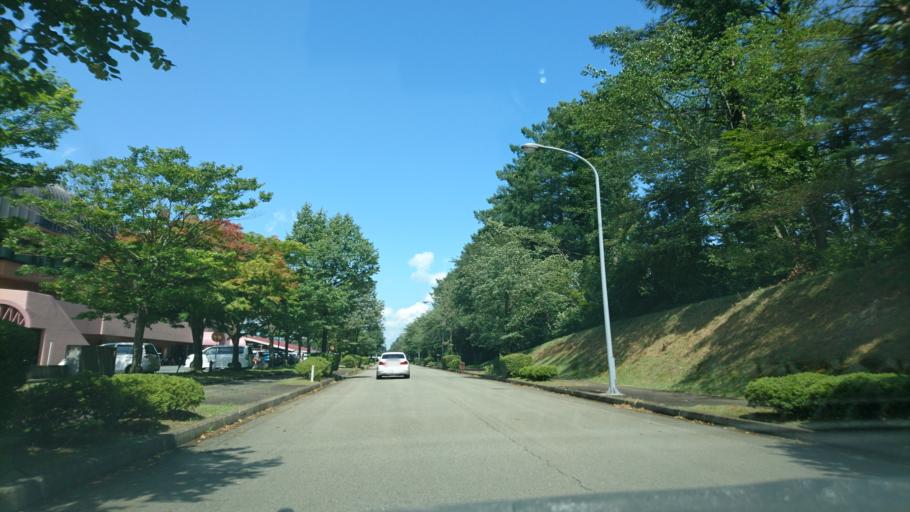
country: JP
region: Iwate
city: Morioka-shi
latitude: 39.8079
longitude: 141.1327
